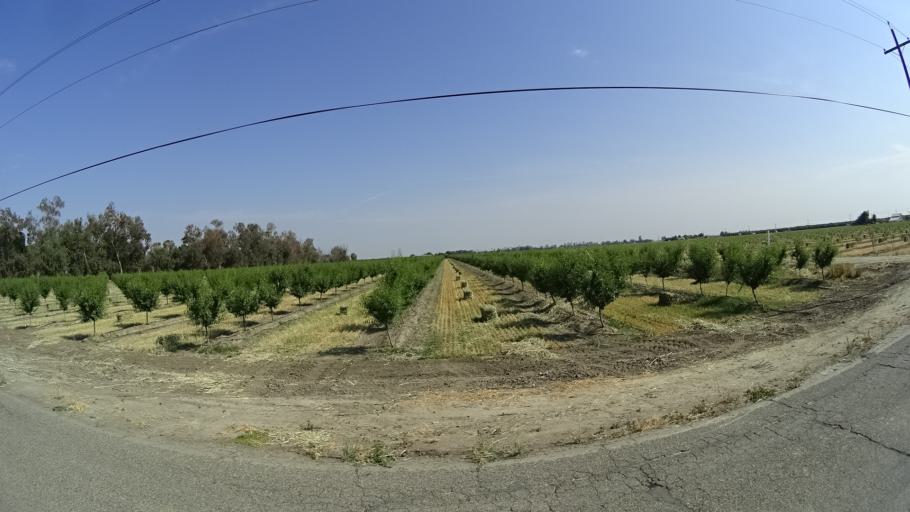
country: US
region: California
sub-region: Kings County
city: Lemoore
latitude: 36.3132
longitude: -119.8125
